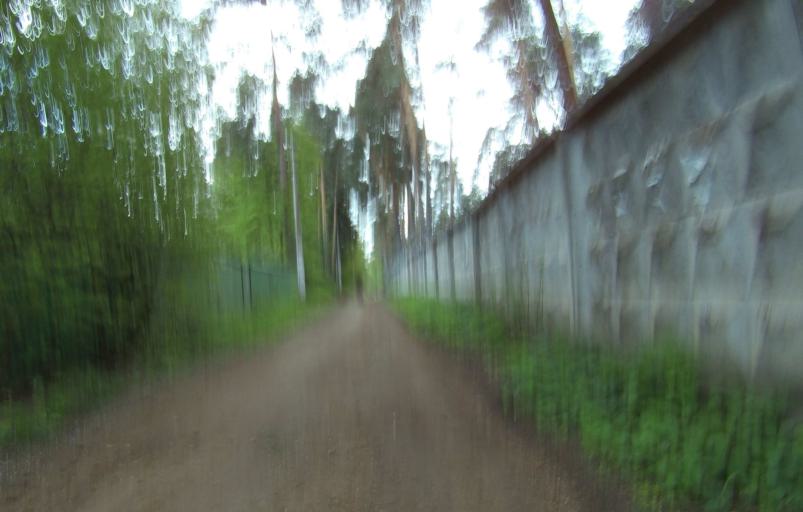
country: RU
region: Moskovskaya
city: Kratovo
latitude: 55.5901
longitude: 38.1814
